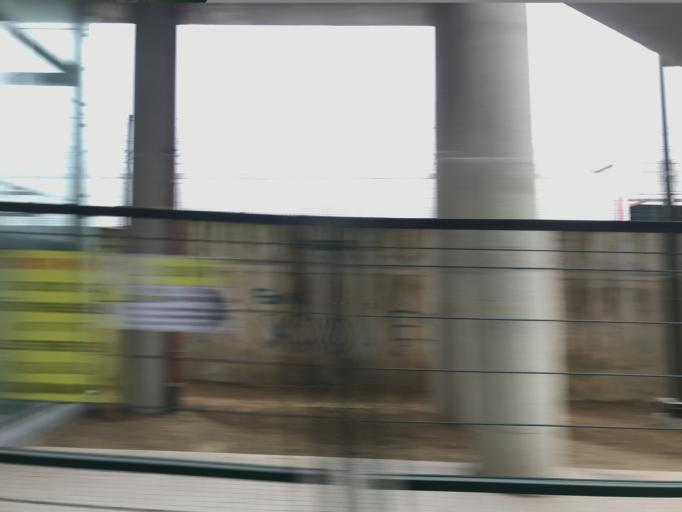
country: TR
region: Kocaeli
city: Darica
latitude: 40.7992
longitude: 29.3804
